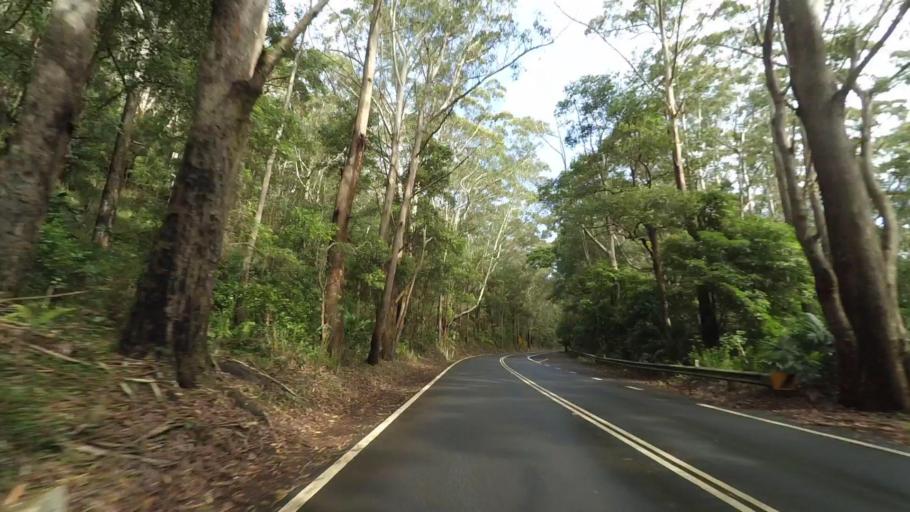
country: AU
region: New South Wales
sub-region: Wollongong
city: Helensburgh
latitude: -34.2053
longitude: 151.0109
